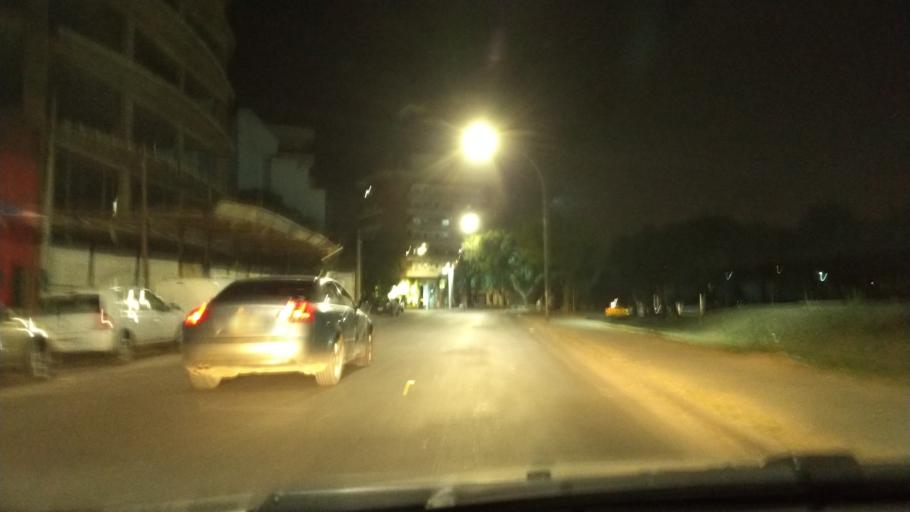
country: AR
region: Cordoba
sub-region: Departamento de Capital
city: Cordoba
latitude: -31.4112
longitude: -64.1733
